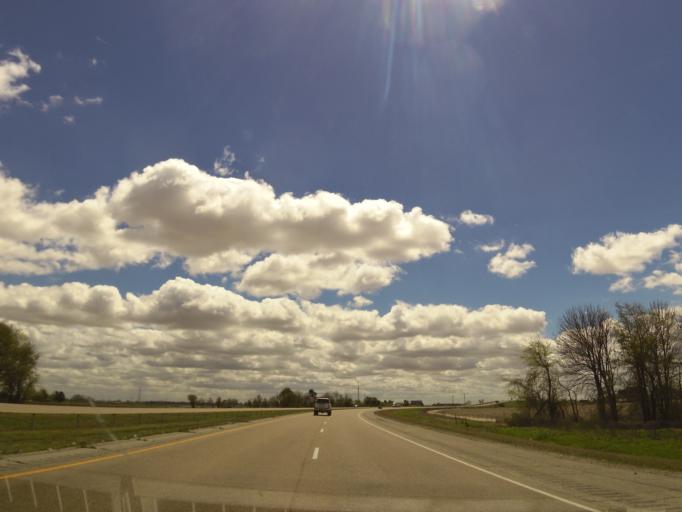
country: US
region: Arkansas
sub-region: Craighead County
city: Bay
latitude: 35.7678
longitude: -90.5773
